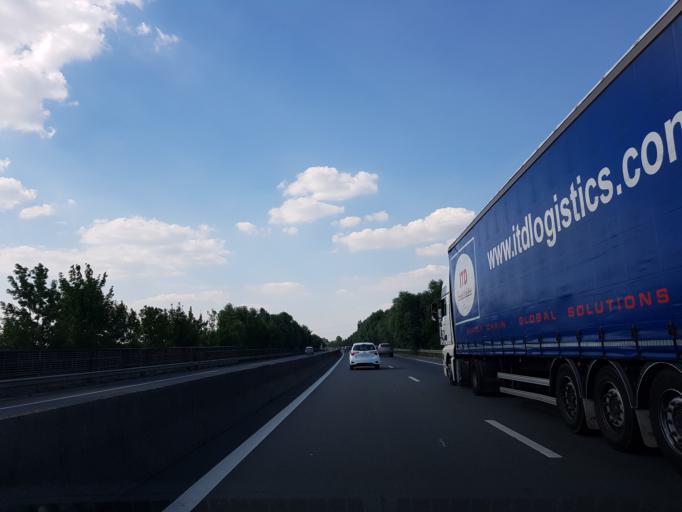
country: FR
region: Nord-Pas-de-Calais
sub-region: Departement du Nord
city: Bruille-lez-Marchiennes
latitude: 50.3604
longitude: 3.2624
